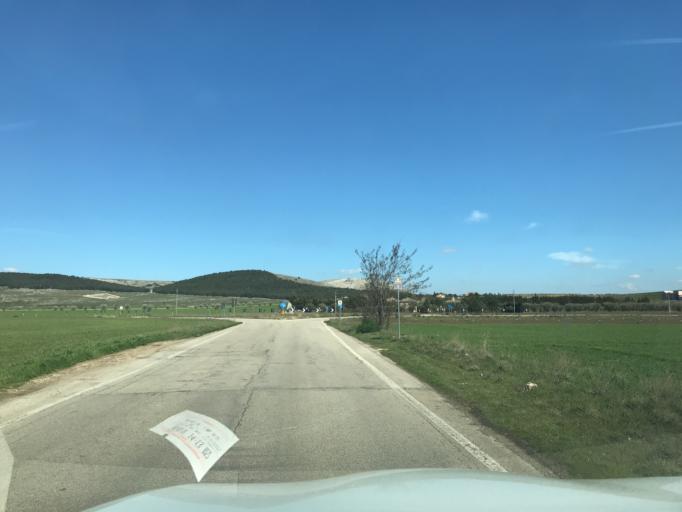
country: IT
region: Apulia
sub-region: Provincia di Bari
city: Gravina in Puglia
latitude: 40.8596
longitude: 16.4356
